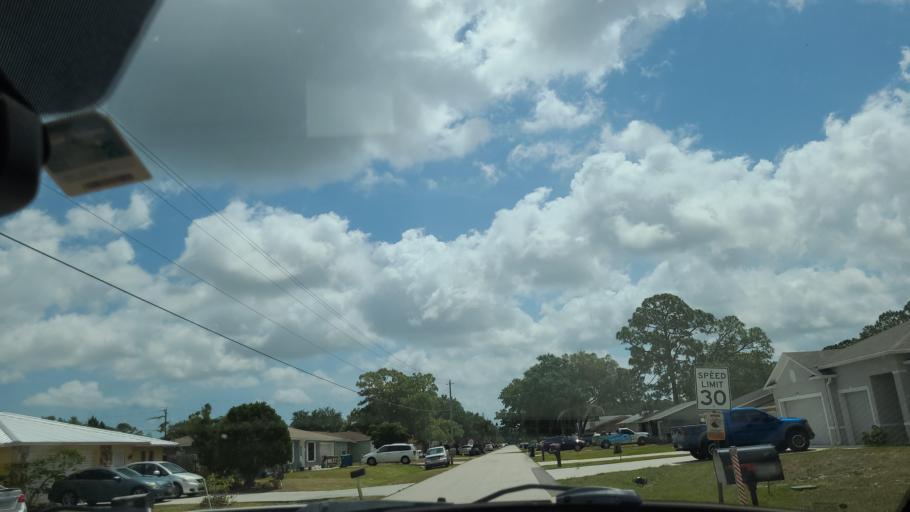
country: US
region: Florida
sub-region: Brevard County
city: June Park
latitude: 28.0058
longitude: -80.6846
